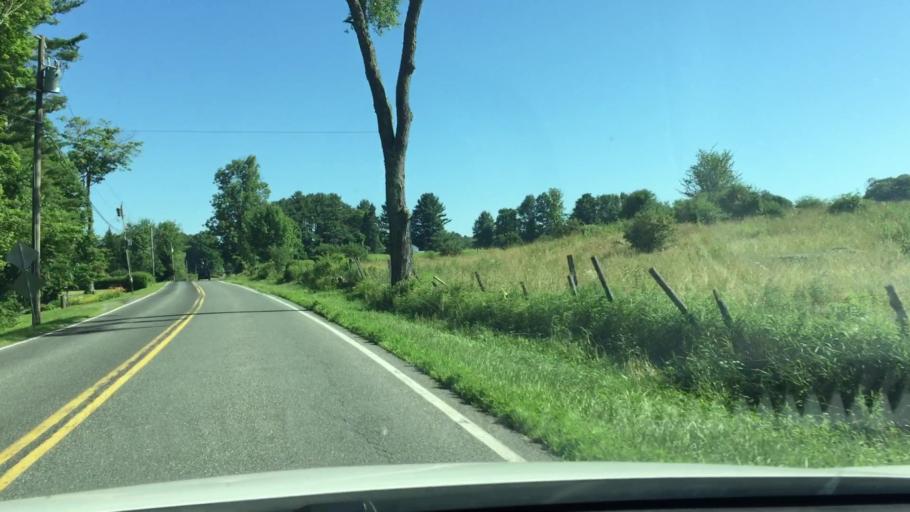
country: US
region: Massachusetts
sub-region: Berkshire County
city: Richmond
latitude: 42.3747
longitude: -73.3456
